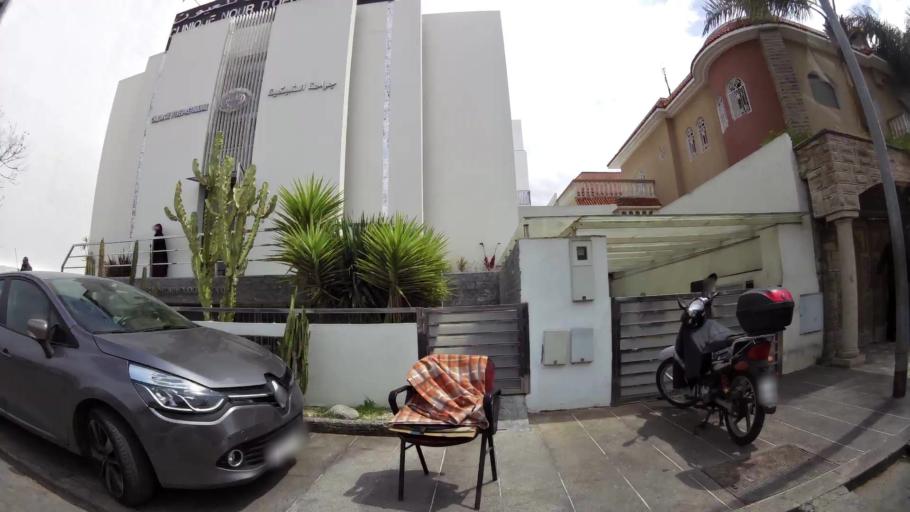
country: MA
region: Grand Casablanca
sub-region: Casablanca
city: Casablanca
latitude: 33.5538
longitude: -7.6439
